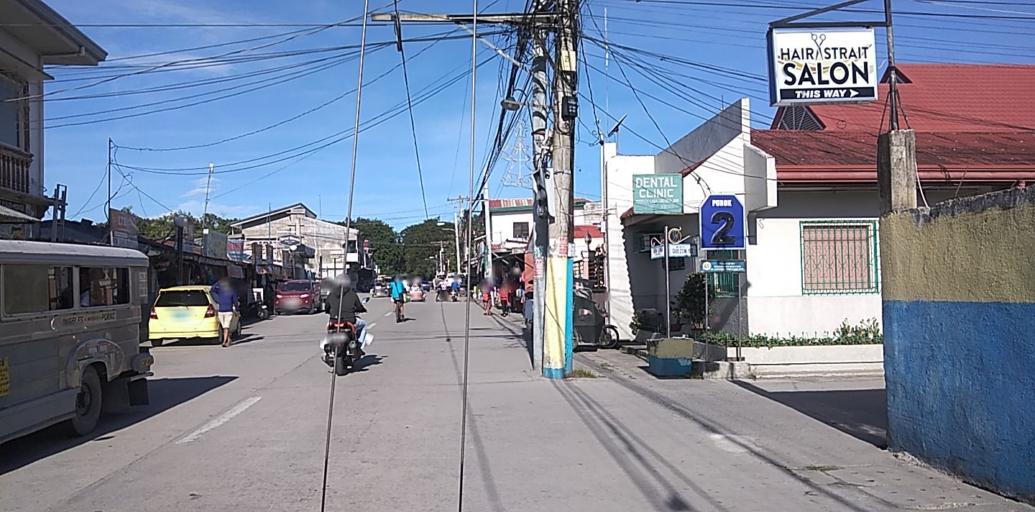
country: PH
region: Central Luzon
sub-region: Province of Pampanga
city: Porac
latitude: 15.0727
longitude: 120.5415
